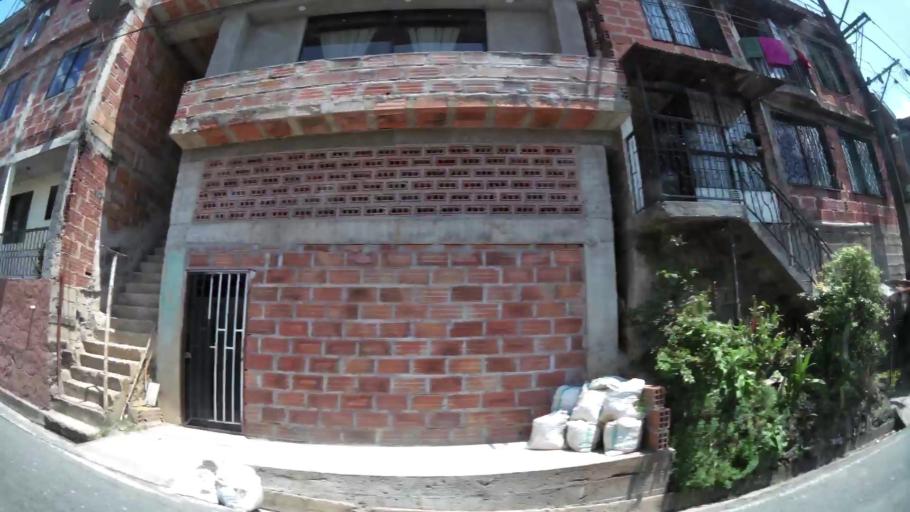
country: CO
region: Antioquia
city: La Estrella
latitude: 6.1830
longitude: -75.6528
